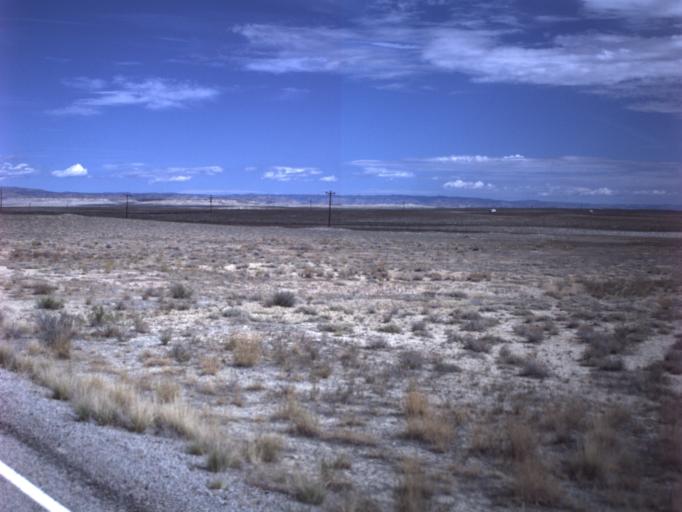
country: US
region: Utah
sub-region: Grand County
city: Moab
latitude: 38.9445
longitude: -109.3535
